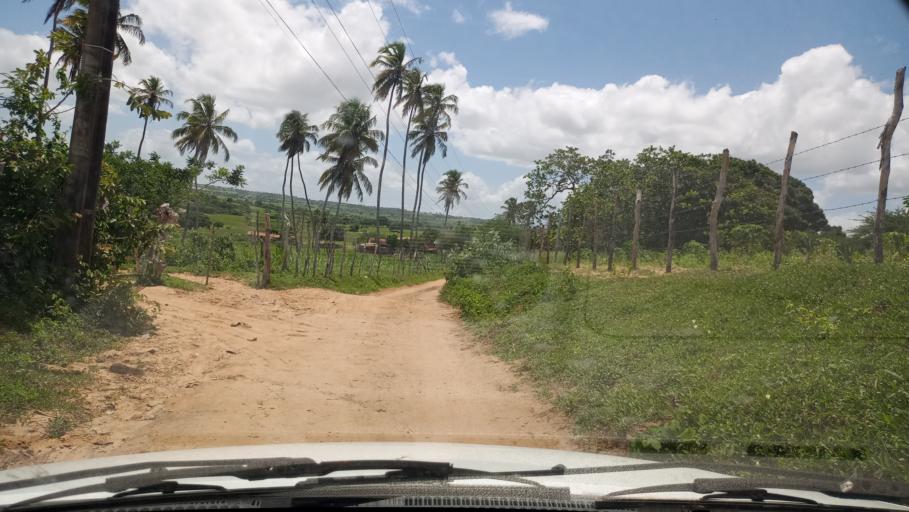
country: BR
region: Rio Grande do Norte
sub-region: Brejinho
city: Brejinho
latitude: -6.2626
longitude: -35.3741
